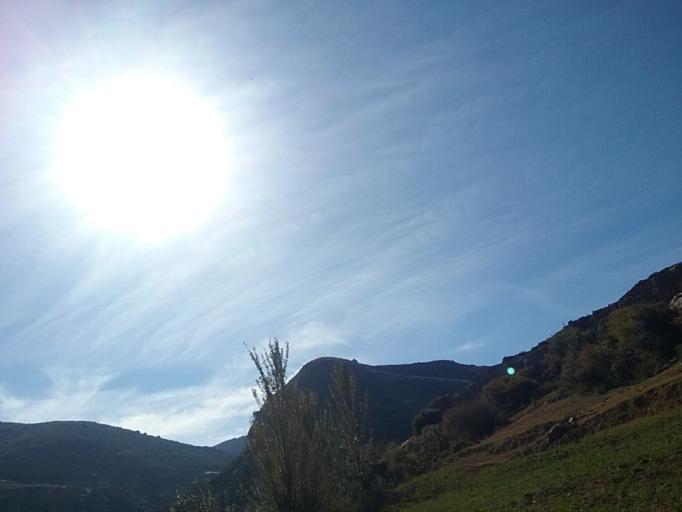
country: LS
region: Berea
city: Teyateyaneng
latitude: -29.2491
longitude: 27.9262
